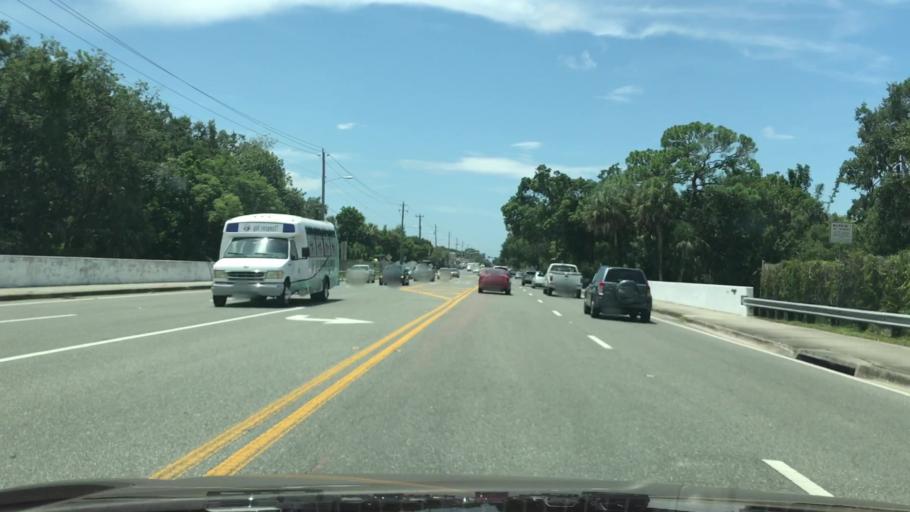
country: US
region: Florida
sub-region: Sarasota County
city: Southgate
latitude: 27.3044
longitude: -82.5142
